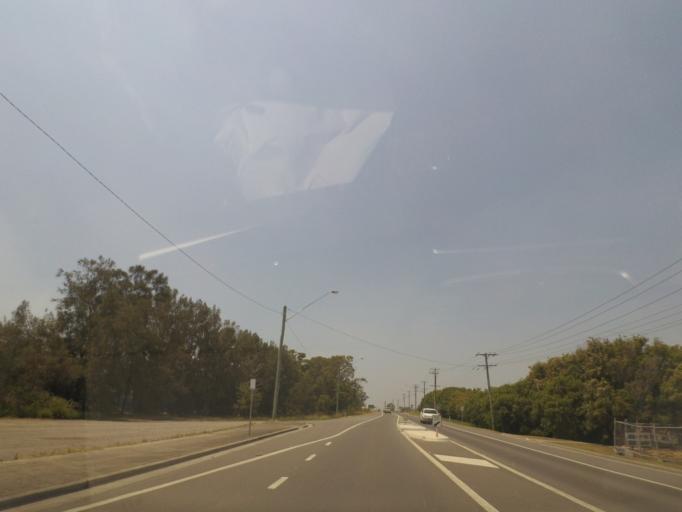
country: AU
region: New South Wales
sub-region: Newcastle
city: Beresfield
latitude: -32.8191
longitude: 151.6983
